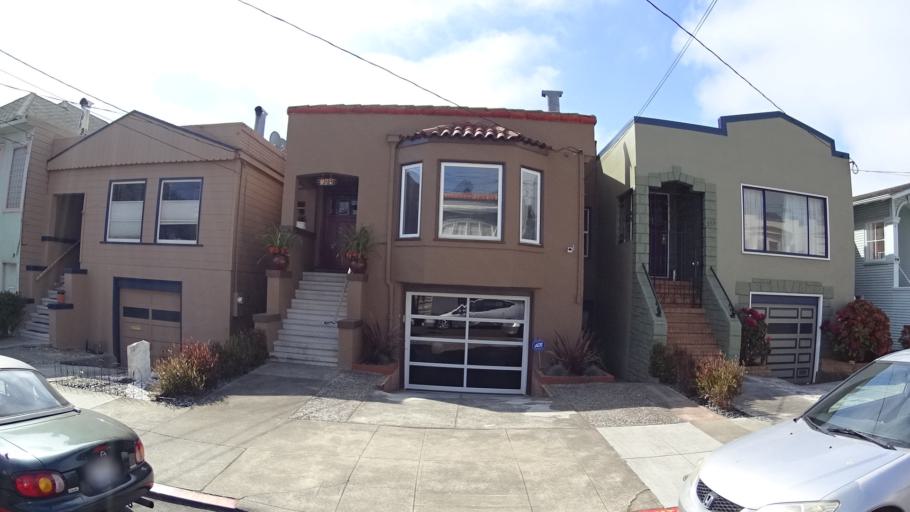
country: US
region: California
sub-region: San Mateo County
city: Daly City
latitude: 37.7298
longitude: -122.4522
